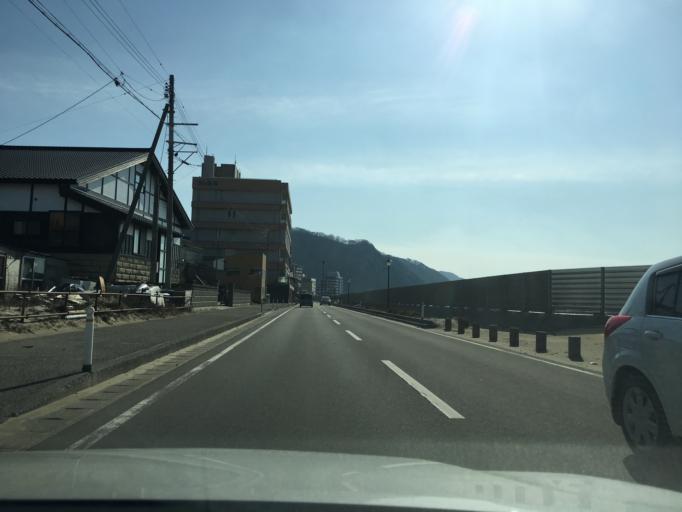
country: JP
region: Yamagata
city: Tsuruoka
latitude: 38.7836
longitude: 139.7532
